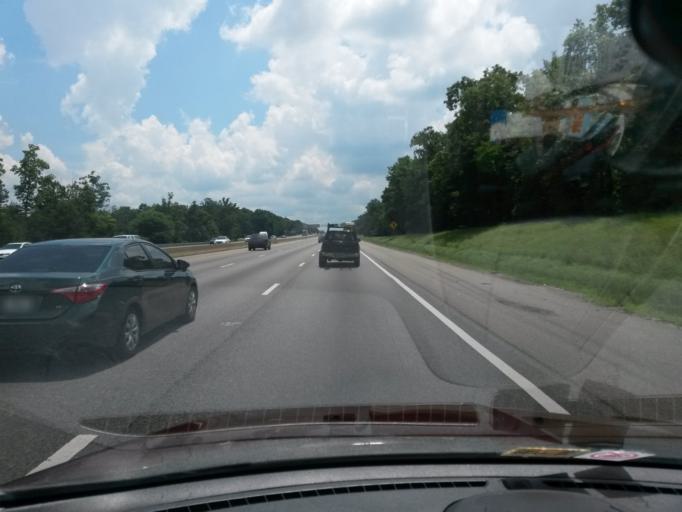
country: US
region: Virginia
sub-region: Chesterfield County
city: Chester
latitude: 37.3594
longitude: -77.4042
